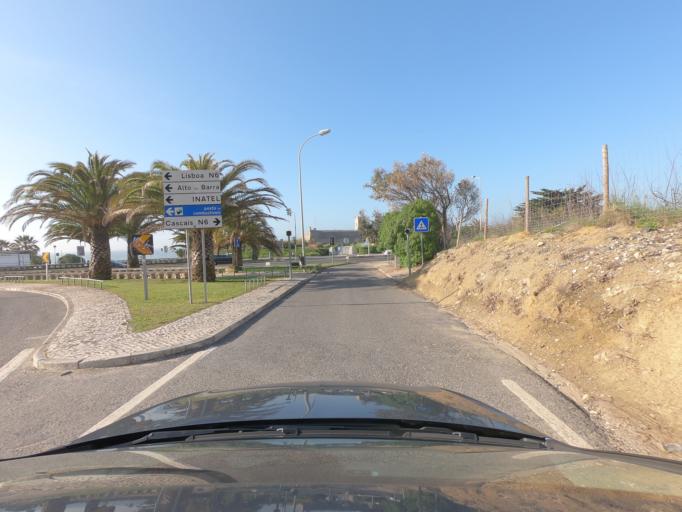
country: PT
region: Lisbon
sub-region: Oeiras
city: Carcavelos
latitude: 38.6775
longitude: -9.3242
